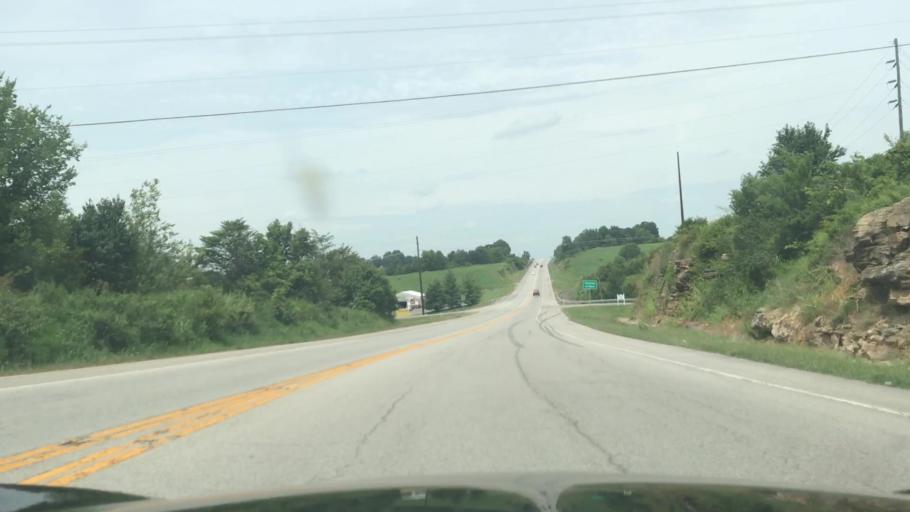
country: US
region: Kentucky
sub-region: Green County
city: Greensburg
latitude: 37.2753
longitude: -85.5098
